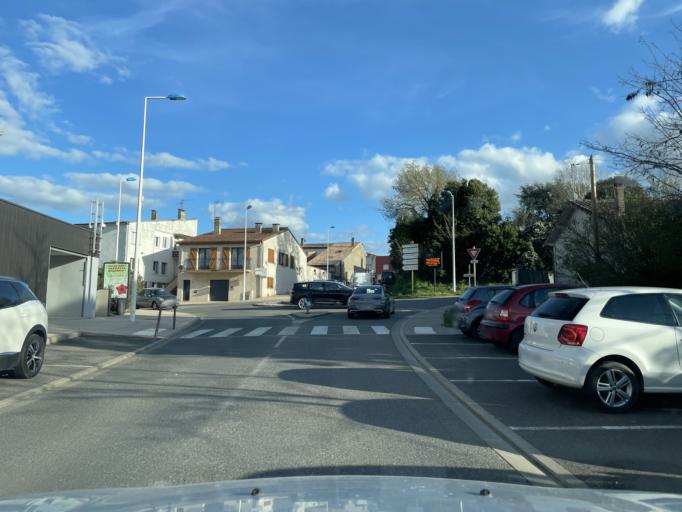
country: FR
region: Midi-Pyrenees
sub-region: Departement de la Haute-Garonne
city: Leguevin
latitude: 43.6006
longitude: 1.2317
